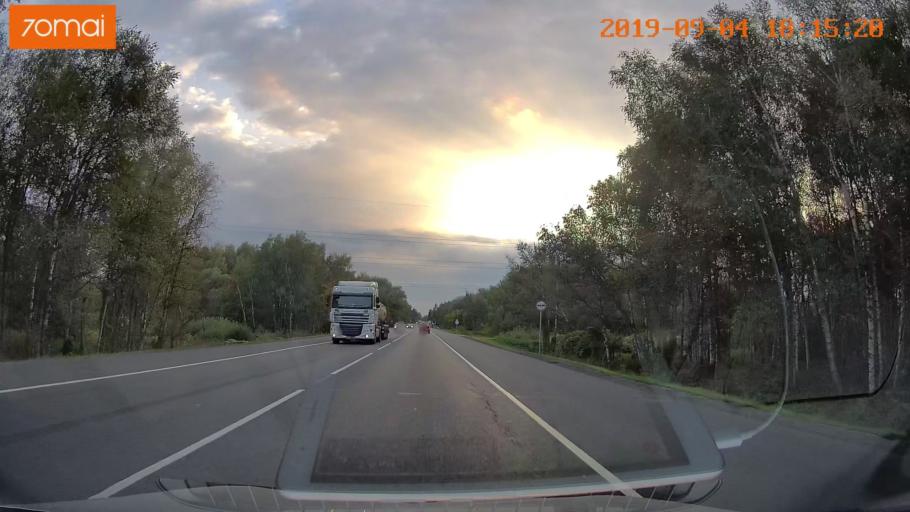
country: RU
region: Moskovskaya
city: Lopatinskiy
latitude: 55.3475
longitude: 38.7046
